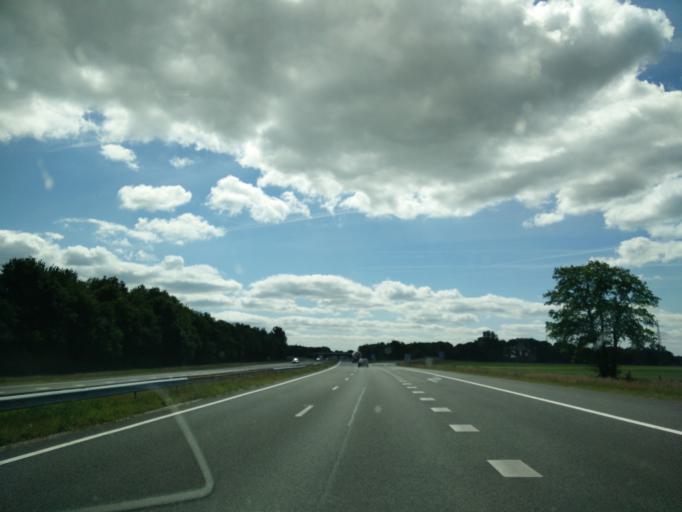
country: NL
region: Drenthe
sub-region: Gemeente Assen
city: Assen
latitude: 52.9787
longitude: 6.5305
